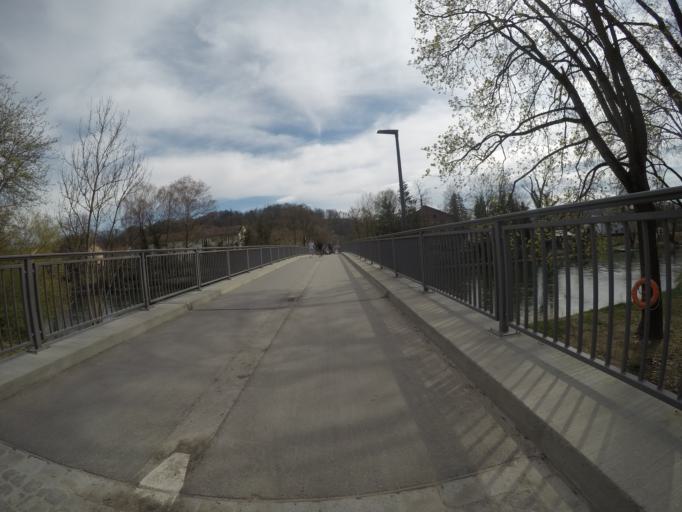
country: DE
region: Bavaria
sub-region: Lower Bavaria
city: Landshut
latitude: 48.5442
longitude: 12.1651
